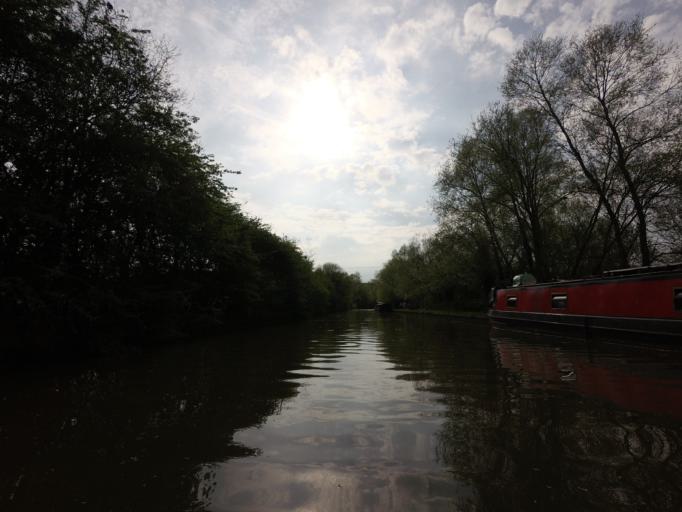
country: GB
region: England
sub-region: Central Bedfordshire
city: Leighton Buzzard
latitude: 51.9280
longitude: -0.6702
